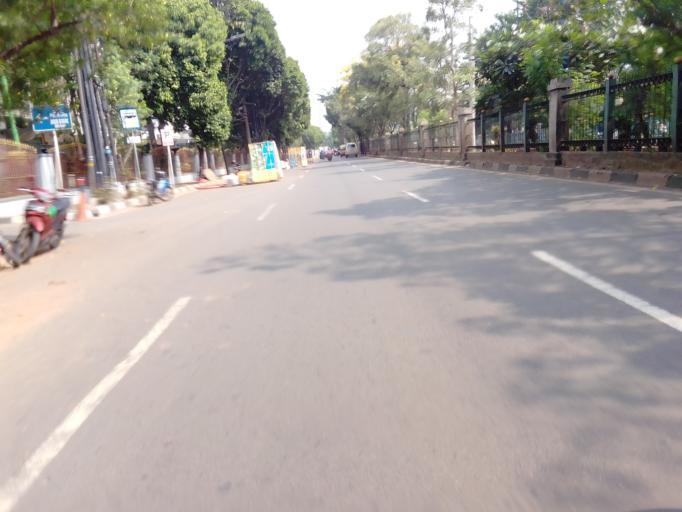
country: ID
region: Jakarta Raya
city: Jakarta
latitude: -6.2197
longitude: 106.7918
